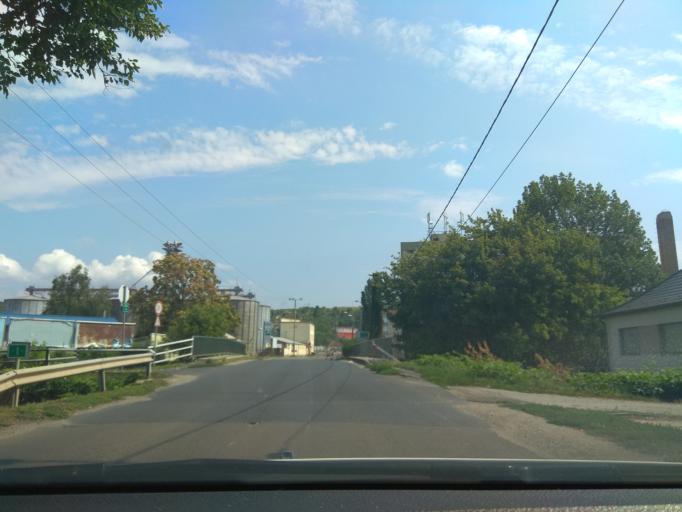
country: HU
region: Heves
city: Eger
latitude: 47.8877
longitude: 20.3930
